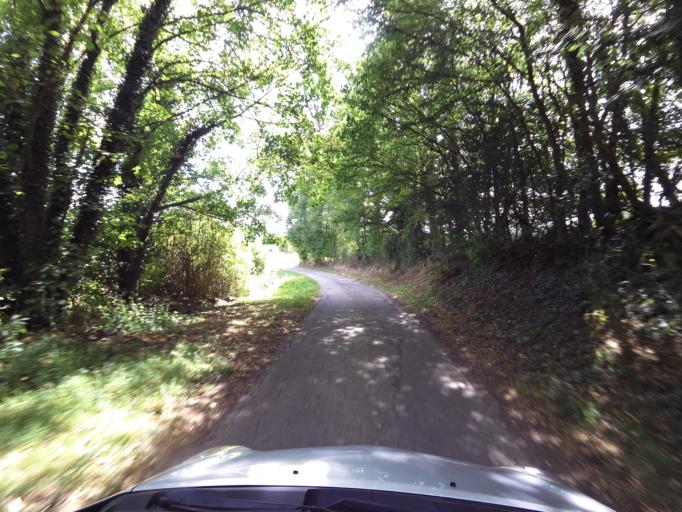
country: FR
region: Picardie
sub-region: Departement de l'Aisne
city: Bruyeres-et-Montberault
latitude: 49.4791
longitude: 3.6404
